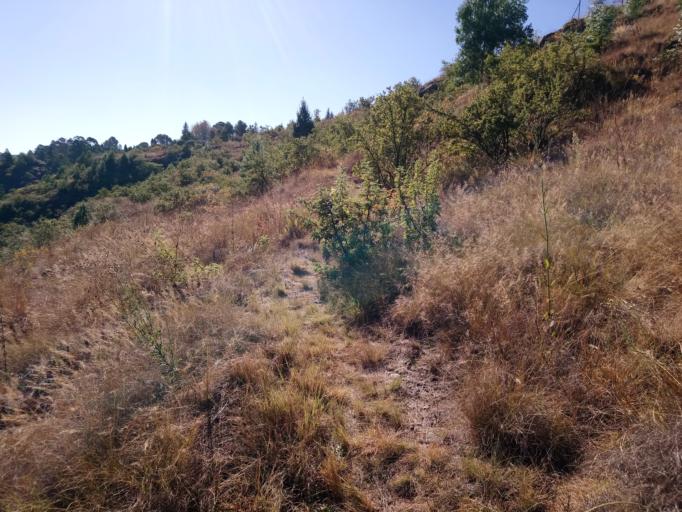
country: ZA
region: KwaZulu-Natal
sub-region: uMgungundlovu District Municipality
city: Mooirivier
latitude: -29.3332
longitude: 29.9185
